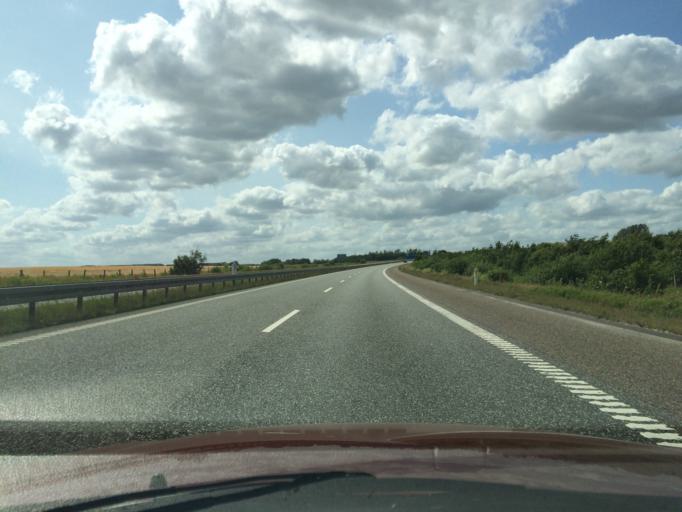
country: DK
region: Central Jutland
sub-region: Skanderborg Kommune
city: Skovby
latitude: 56.1419
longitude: 9.9379
